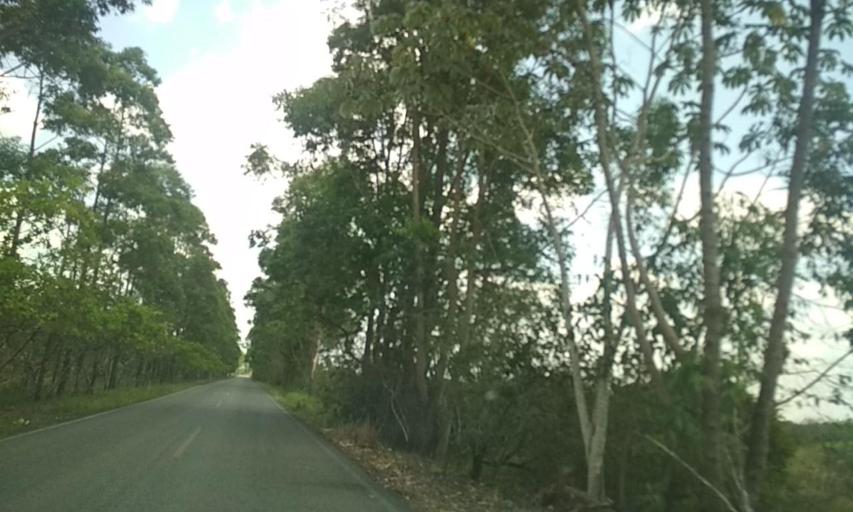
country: MX
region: Tabasco
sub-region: Huimanguillo
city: Francisco Rueda
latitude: 17.7638
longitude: -93.7893
